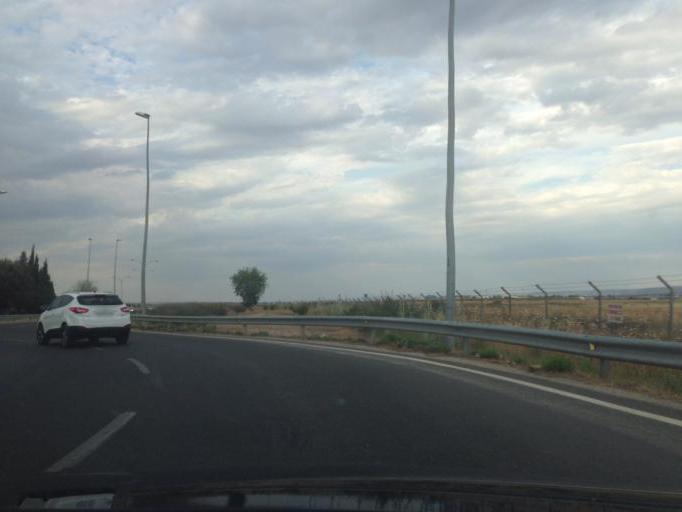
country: ES
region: Madrid
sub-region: Provincia de Madrid
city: Torrejon de Ardoz
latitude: 40.4734
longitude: -3.4792
